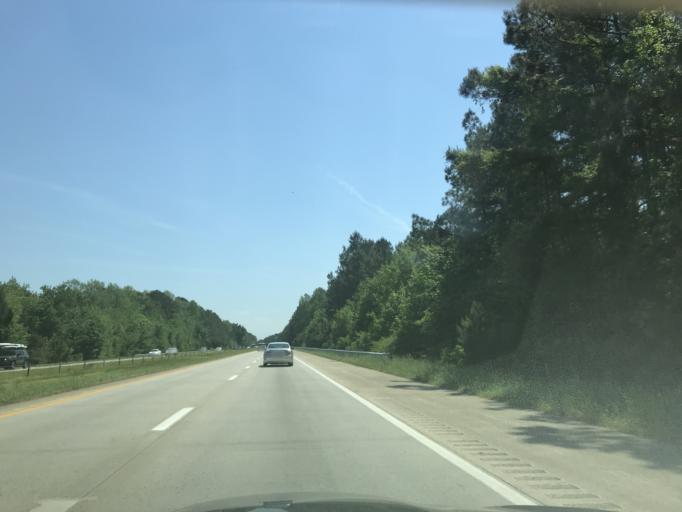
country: US
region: North Carolina
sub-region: Johnston County
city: Benson
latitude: 35.4815
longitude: -78.5510
